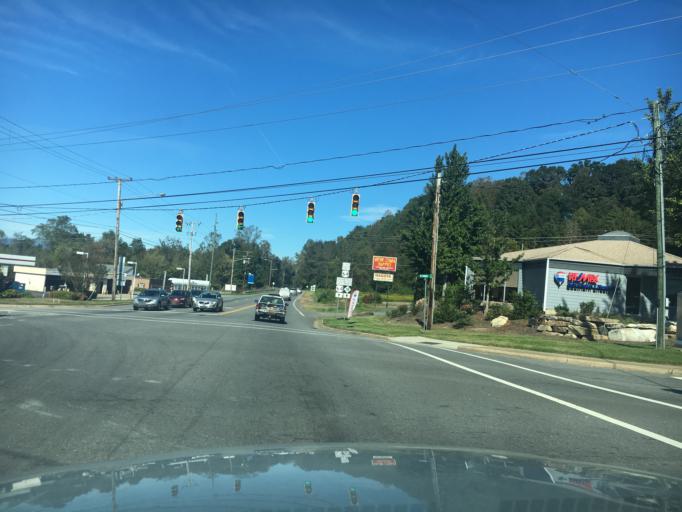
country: US
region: North Carolina
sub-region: Burke County
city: Morganton
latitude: 35.7351
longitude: -81.7088
